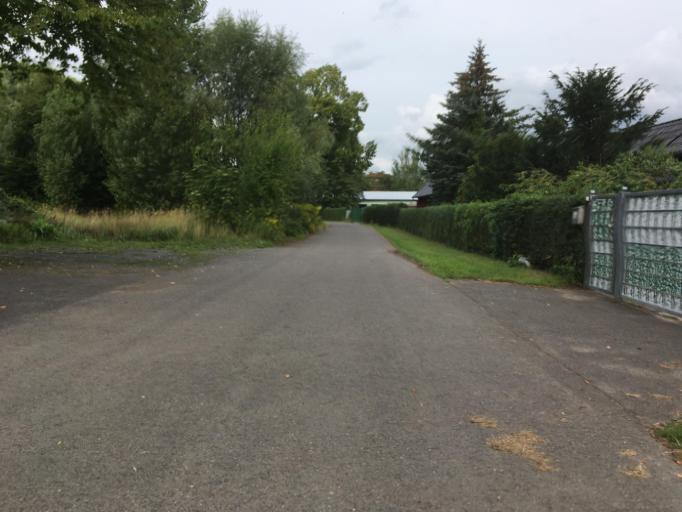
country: DE
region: Brandenburg
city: Prenzlau
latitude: 53.3049
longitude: 13.8454
